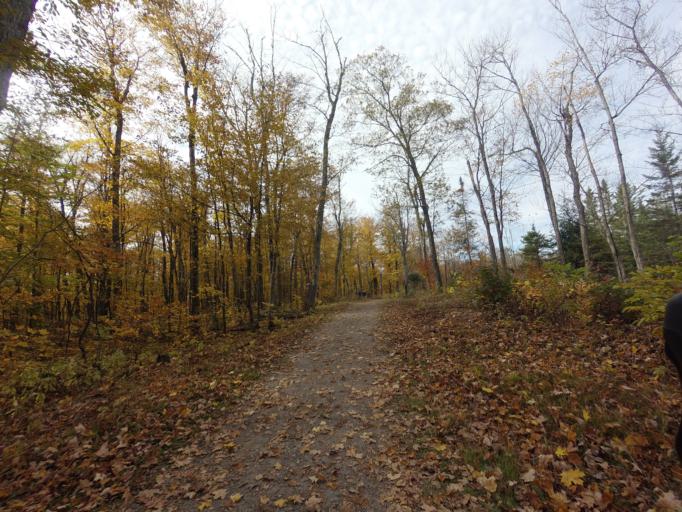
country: CA
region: Quebec
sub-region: Outaouais
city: Wakefield
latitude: 45.5102
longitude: -75.9080
